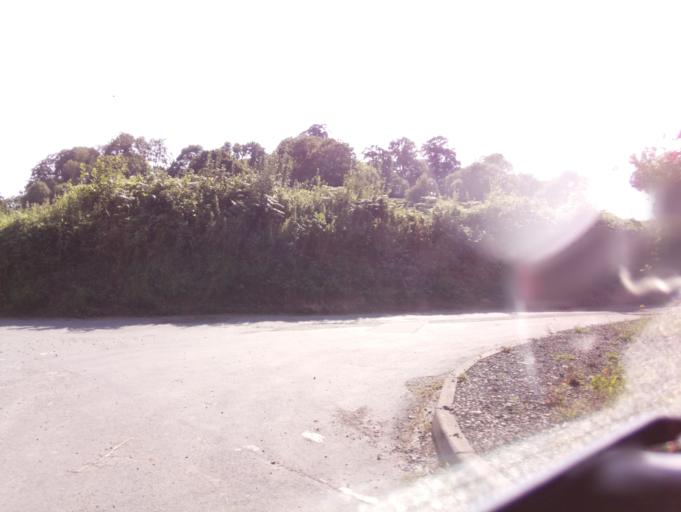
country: GB
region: England
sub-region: Gloucestershire
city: Dursley
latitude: 51.6868
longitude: -2.3203
